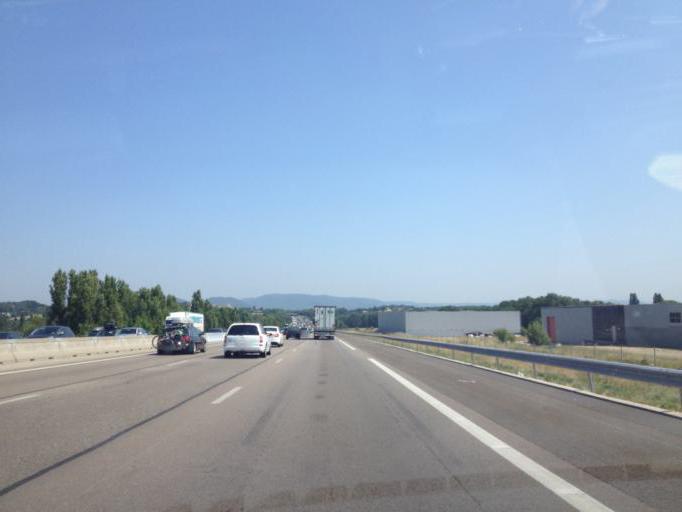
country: FR
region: Rhone-Alpes
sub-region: Departement de la Drome
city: Montboucher-sur-Jabron
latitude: 44.5371
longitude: 4.8046
